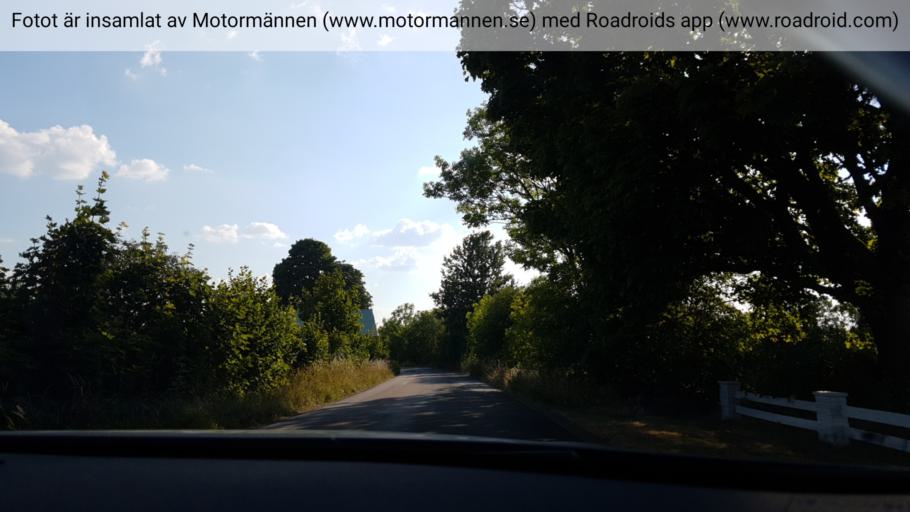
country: SE
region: Vaestra Goetaland
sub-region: Skovde Kommun
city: Stopen
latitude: 58.4929
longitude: 13.7819
